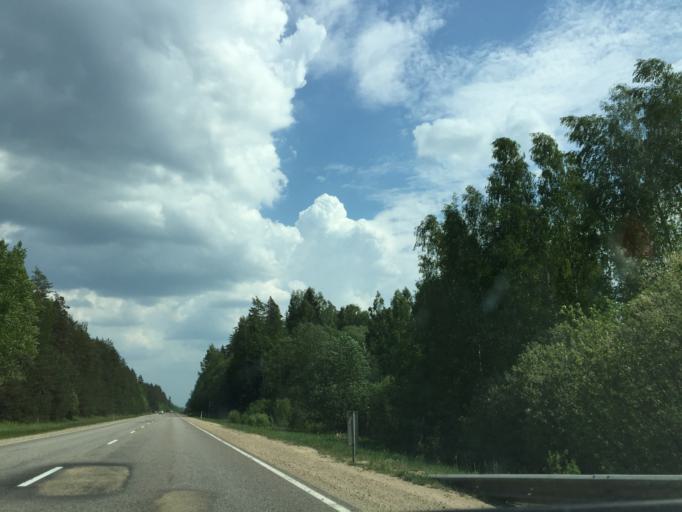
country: LV
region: Plavinu
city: Plavinas
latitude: 56.5884
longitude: 25.5783
